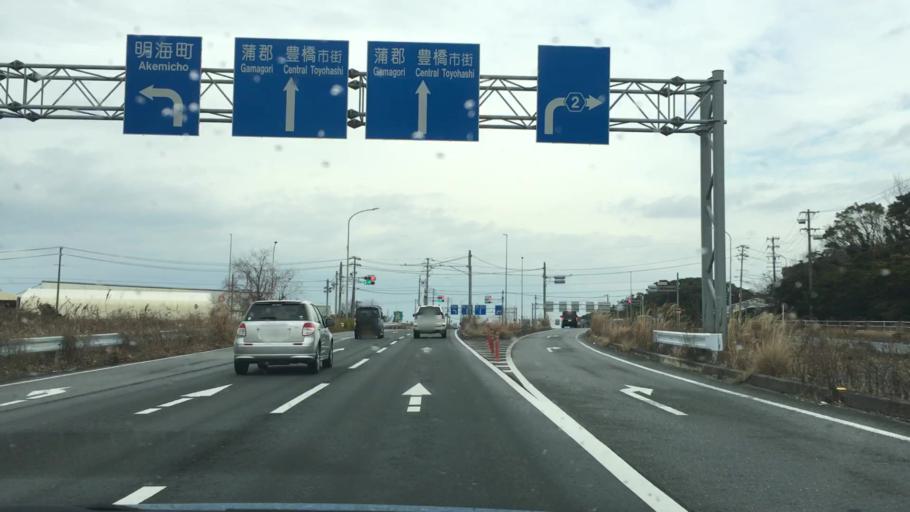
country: JP
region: Aichi
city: Toyohashi
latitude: 34.7176
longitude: 137.3397
